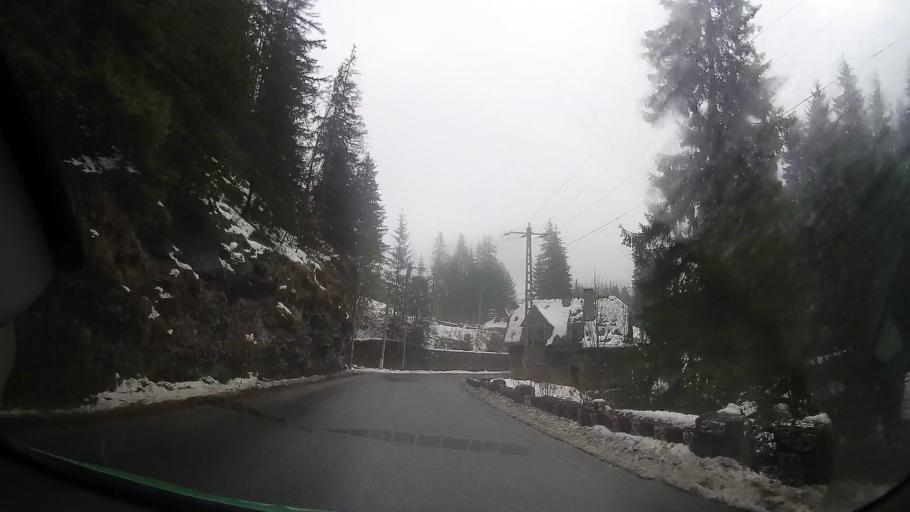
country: RO
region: Neamt
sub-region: Comuna Bicaz Chei
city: Bicaz Chei
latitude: 46.7981
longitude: 25.8018
